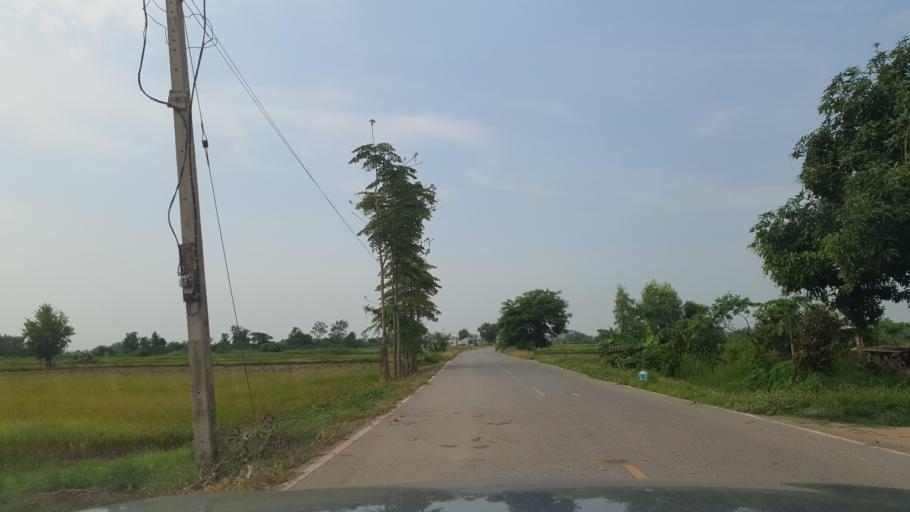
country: TH
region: Phitsanulok
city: Bang Rakam
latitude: 16.8071
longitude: 100.1622
